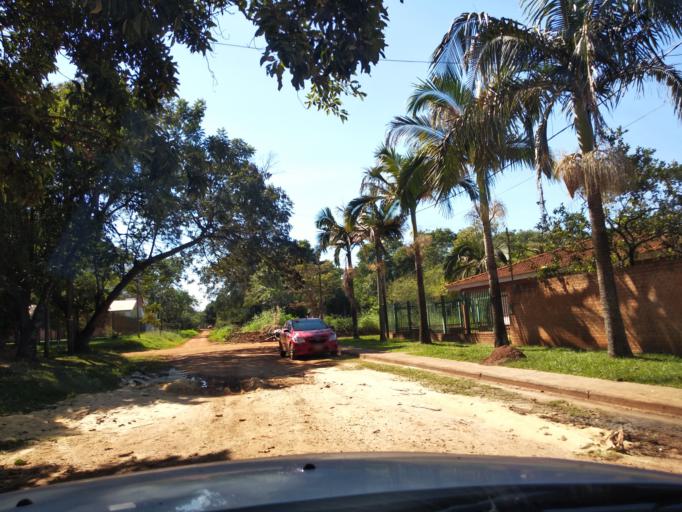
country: AR
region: Misiones
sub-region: Departamento de Capital
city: Posadas
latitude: -27.4315
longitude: -55.8860
